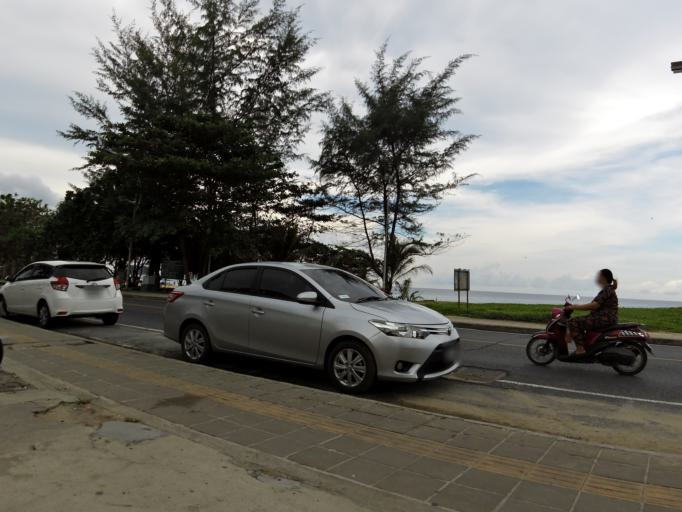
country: TH
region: Phuket
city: Ban Karon
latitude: 7.8446
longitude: 98.2942
